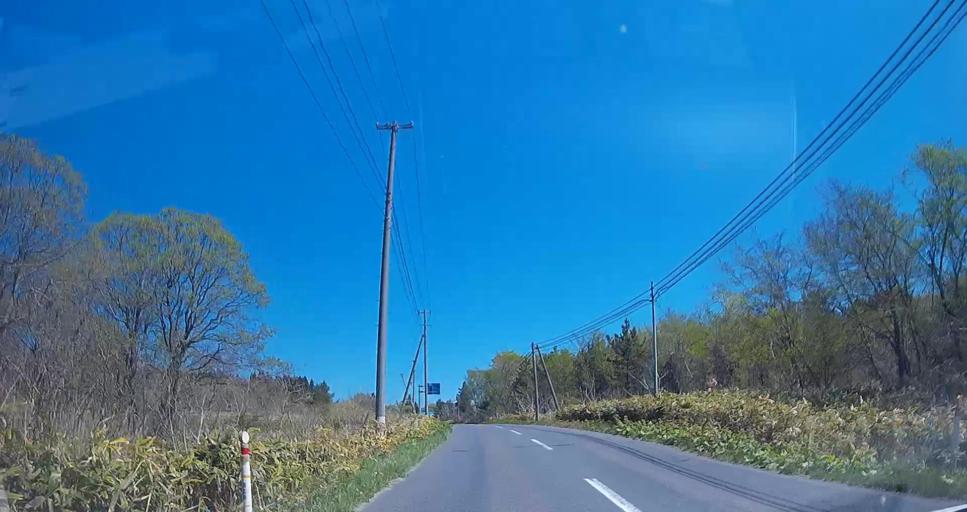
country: JP
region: Aomori
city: Misawa
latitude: 40.9191
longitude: 141.3775
